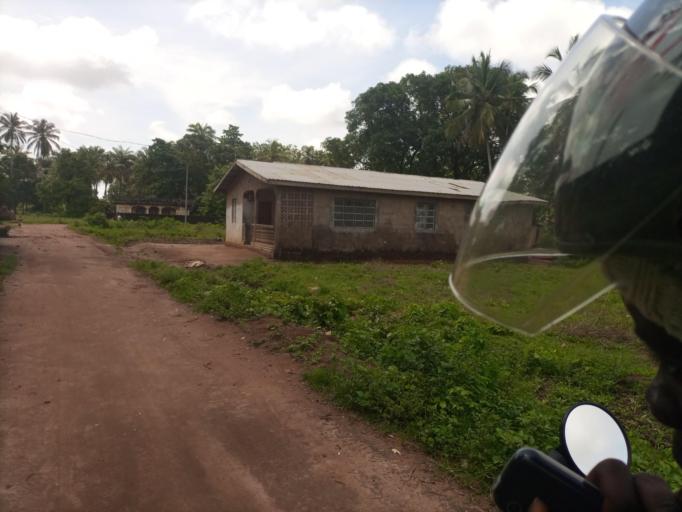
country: SL
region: Northern Province
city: Masoyila
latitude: 8.6196
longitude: -13.1726
